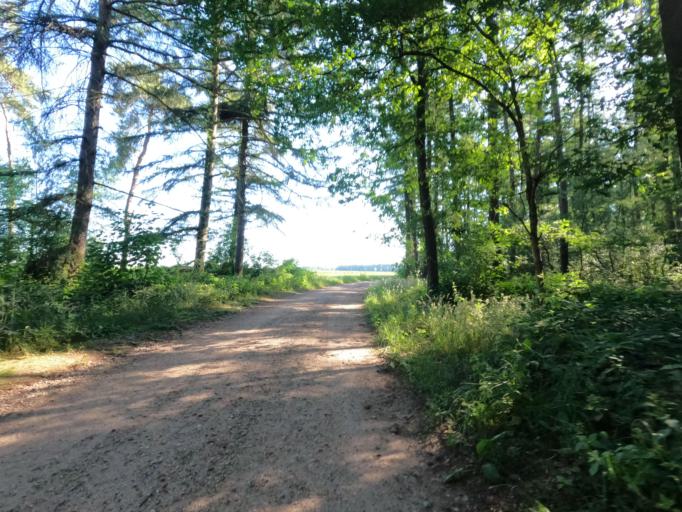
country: NL
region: Limburg
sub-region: Gemeente Roerdalen
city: Vlodrop
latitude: 51.1207
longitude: 6.0656
